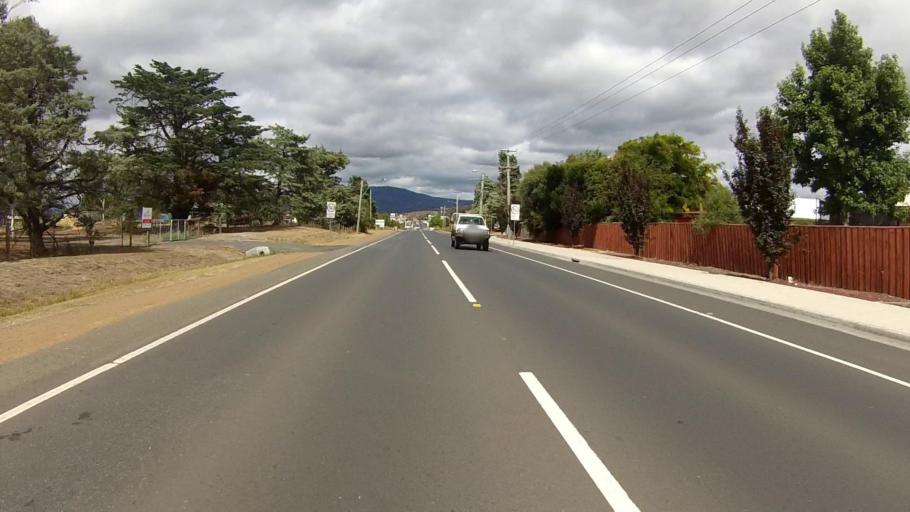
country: AU
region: Tasmania
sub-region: Brighton
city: Bridgewater
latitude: -42.6945
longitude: 147.2562
